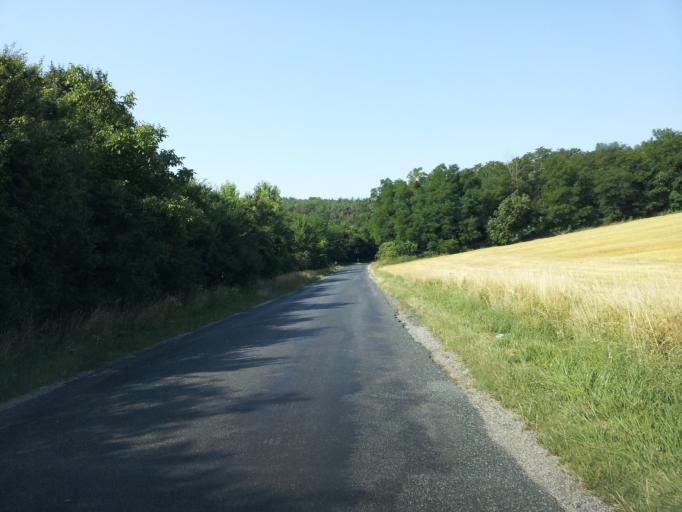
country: HU
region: Zala
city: Heviz
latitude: 46.8667
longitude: 17.1489
